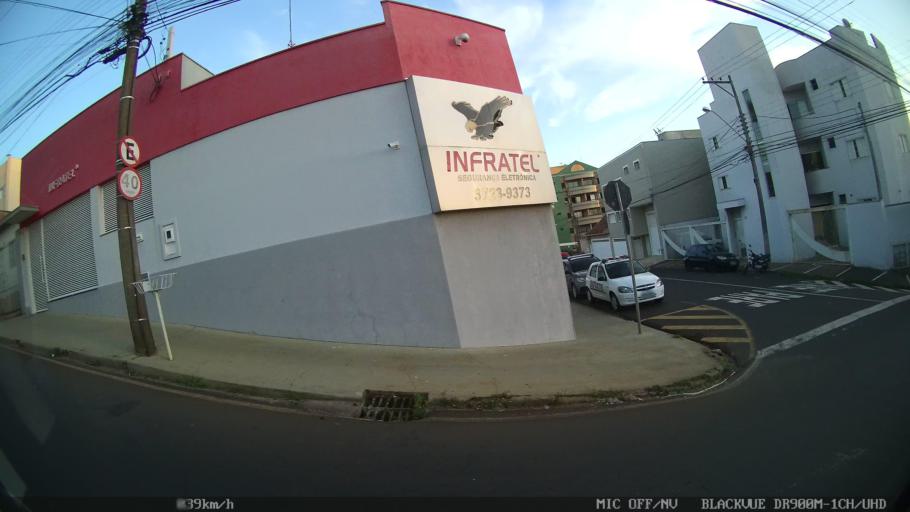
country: BR
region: Sao Paulo
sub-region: Franca
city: Franca
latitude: -20.5498
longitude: -47.4077
